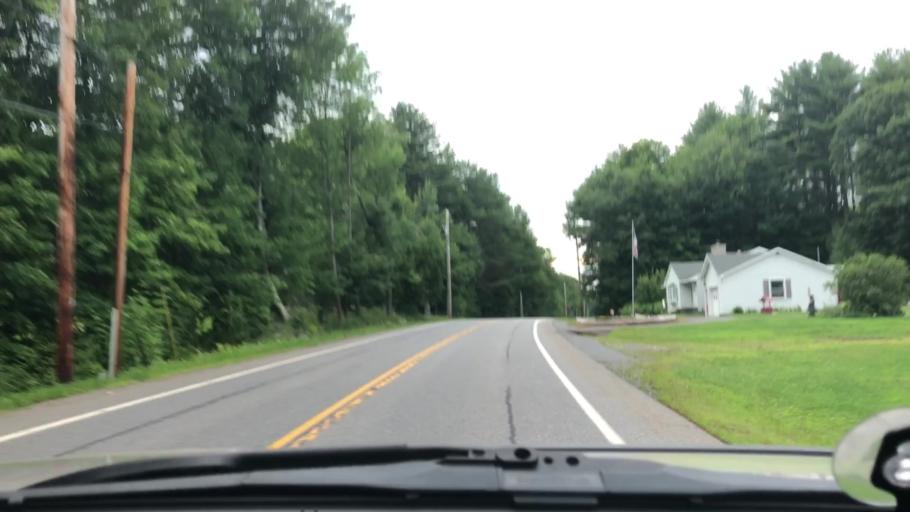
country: US
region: New York
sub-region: Saratoga County
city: Corinth
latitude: 43.2107
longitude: -73.7942
